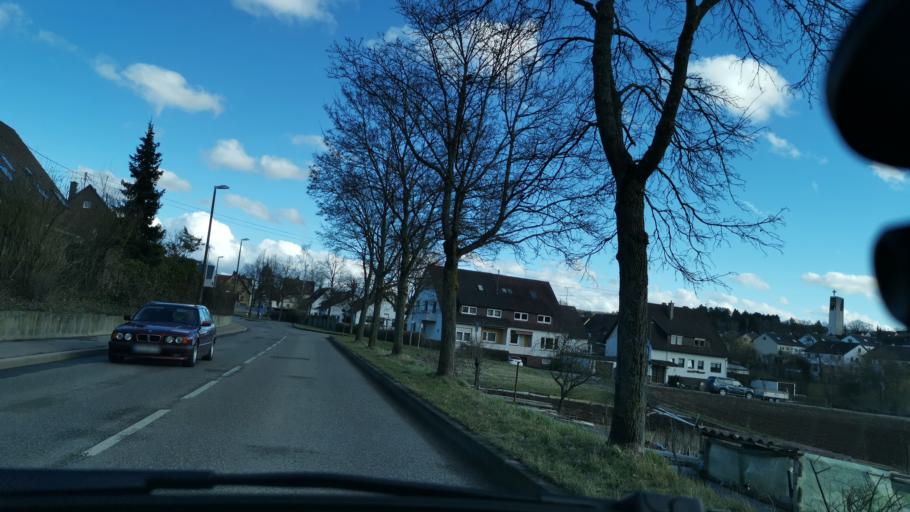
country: DE
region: Baden-Wuerttemberg
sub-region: Regierungsbezirk Stuttgart
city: Weil der Stadt
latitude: 48.7771
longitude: 8.8983
